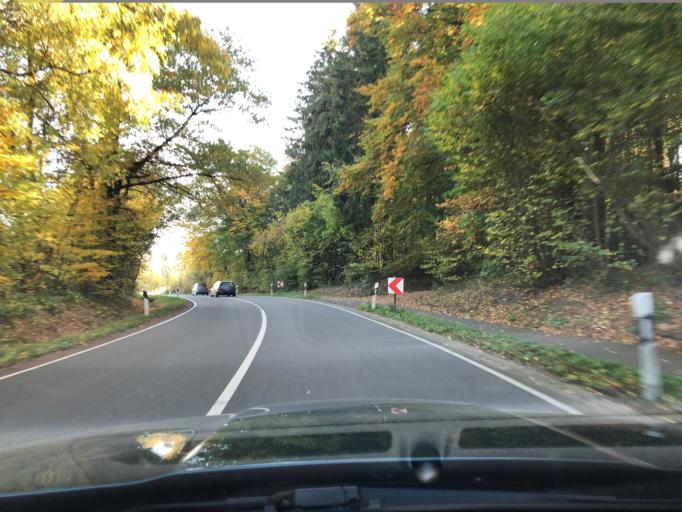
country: DE
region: Lower Saxony
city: Hasbergen
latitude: 52.2025
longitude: 7.9071
